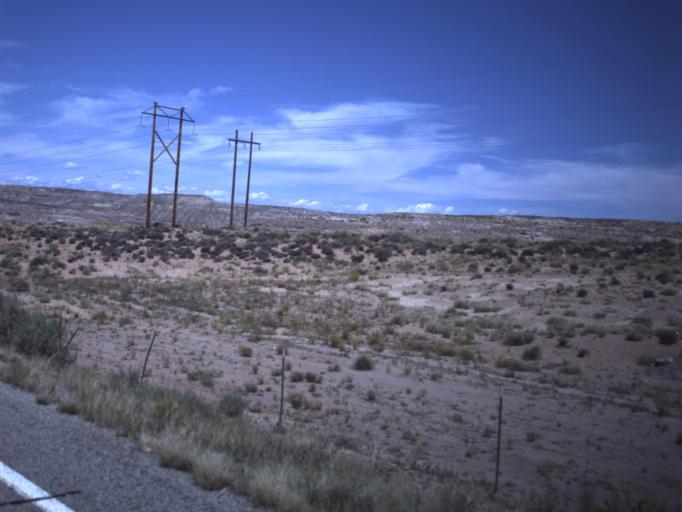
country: US
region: Utah
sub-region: San Juan County
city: Blanding
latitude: 37.2857
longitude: -109.3867
